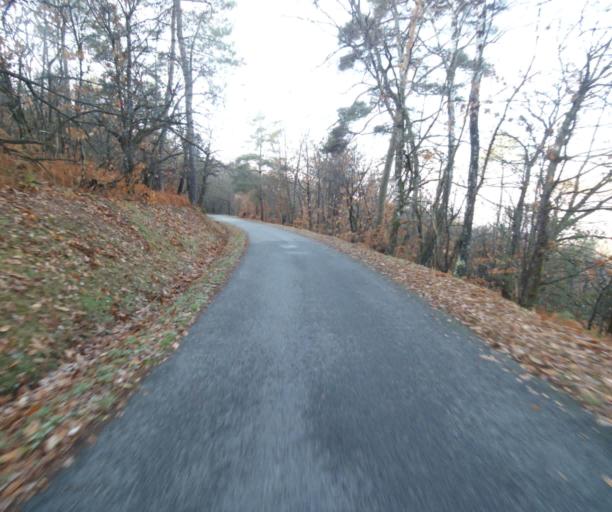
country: FR
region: Limousin
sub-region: Departement de la Correze
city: Laguenne
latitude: 45.2636
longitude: 1.7988
